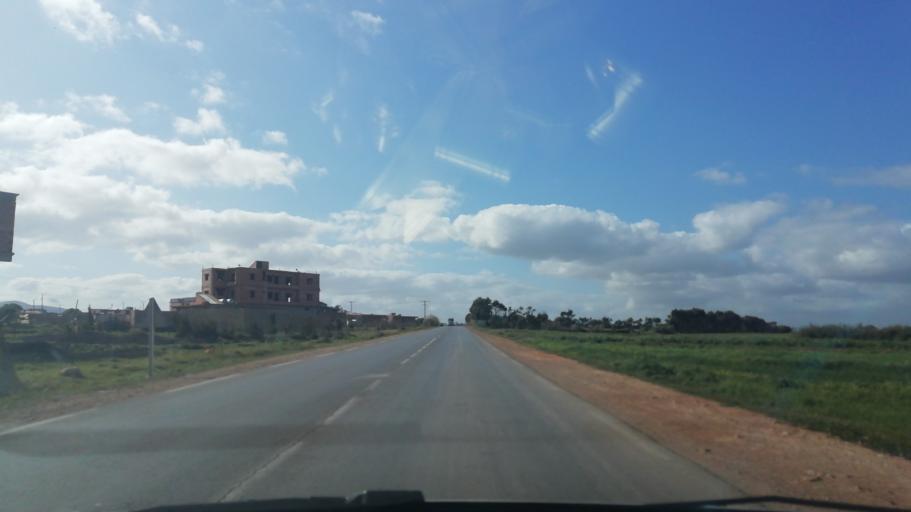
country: DZ
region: Relizane
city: Mazouna
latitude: 36.3280
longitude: 0.6878
